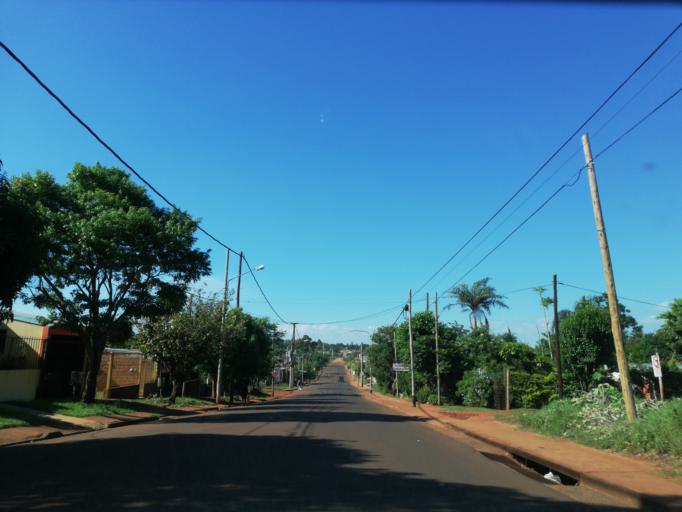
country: AR
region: Misiones
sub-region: Departamento de Capital
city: Posadas
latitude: -27.4252
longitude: -55.9507
